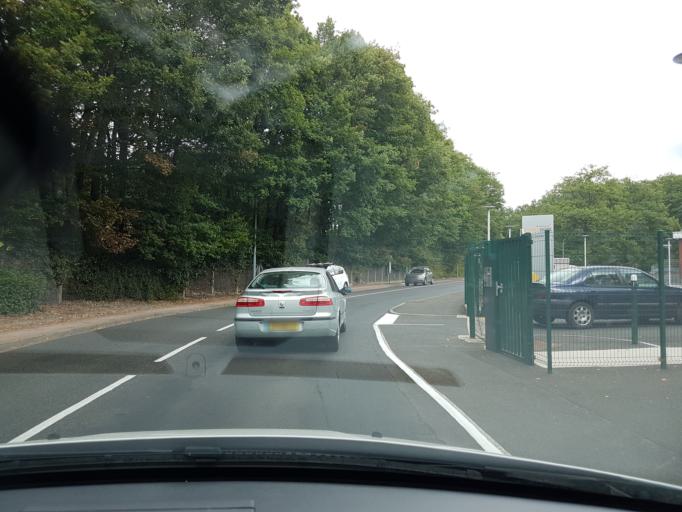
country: FR
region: Centre
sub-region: Departement d'Indre-et-Loire
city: Chambray-les-Tours
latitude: 47.3392
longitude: 0.7176
